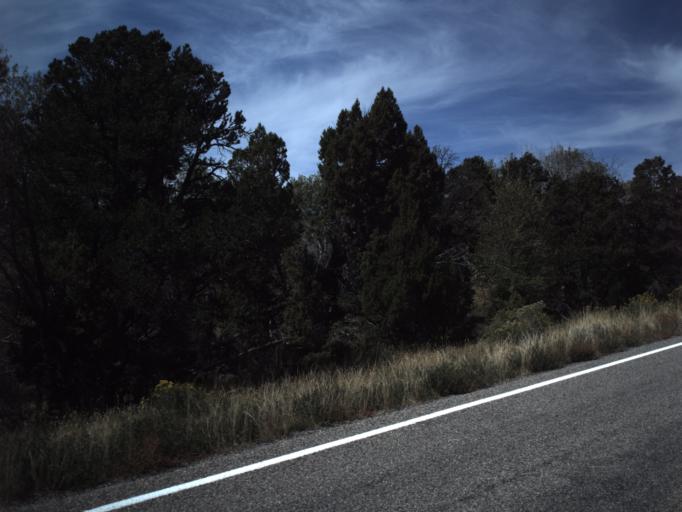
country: US
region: Utah
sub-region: Wayne County
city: Loa
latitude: 37.9305
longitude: -111.4293
